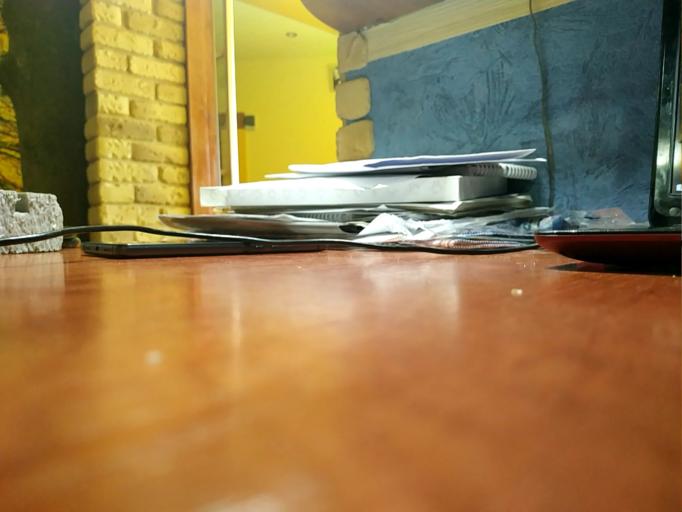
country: RU
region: Vologda
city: Khokhlovo
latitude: 59.4386
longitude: 37.3372
